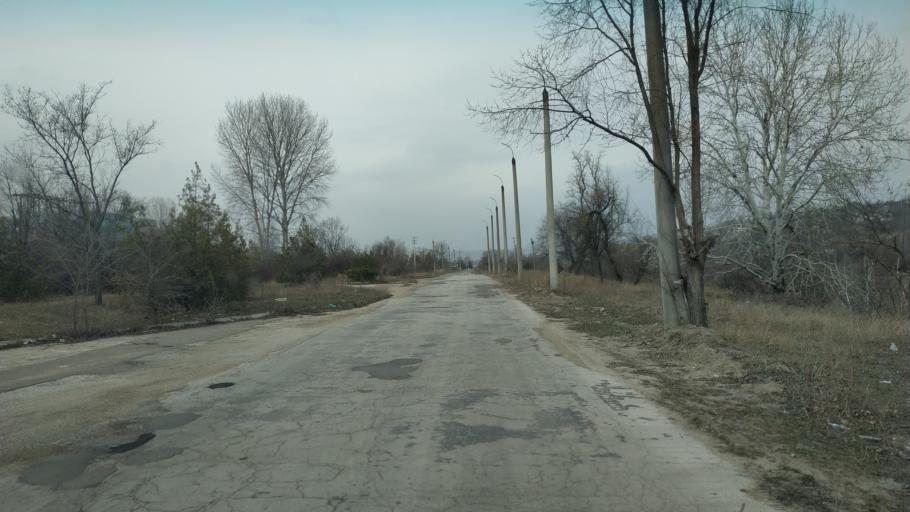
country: MD
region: Chisinau
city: Singera
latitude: 46.9044
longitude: 29.0189
